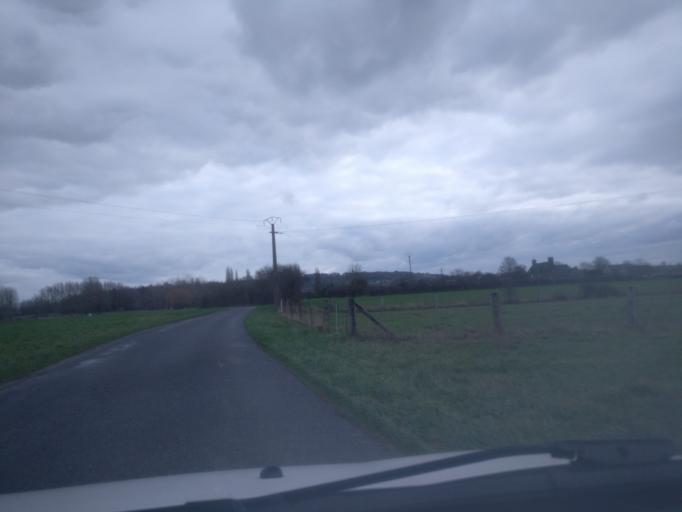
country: FR
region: Lower Normandy
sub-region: Departement de la Manche
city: Marcey-les-Greves
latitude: 48.6751
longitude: -1.4072
